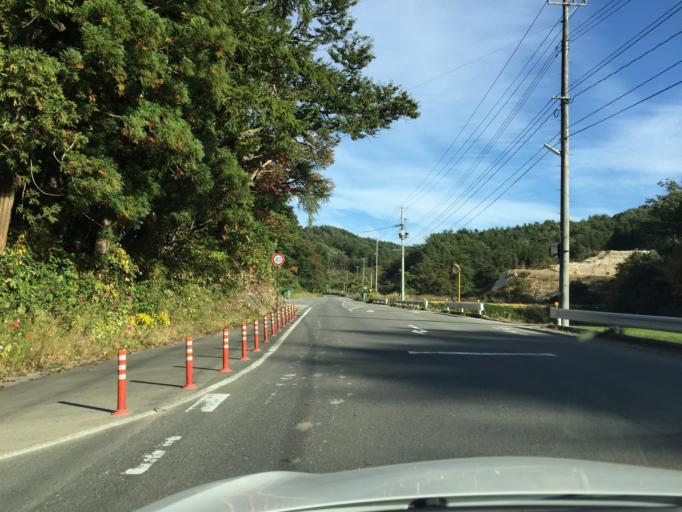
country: JP
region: Fukushima
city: Miharu
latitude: 37.3578
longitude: 140.5384
